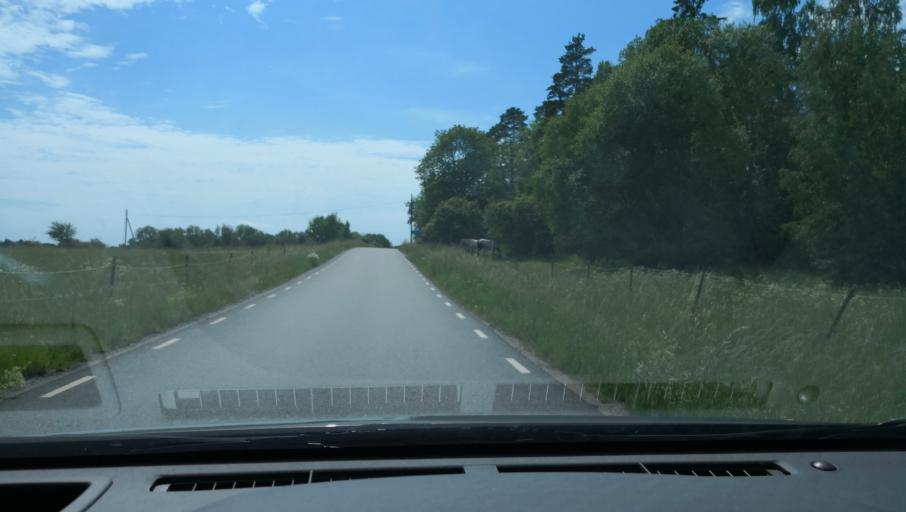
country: SE
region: Uppsala
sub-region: Habo Kommun
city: Balsta
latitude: 59.6886
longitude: 17.4652
